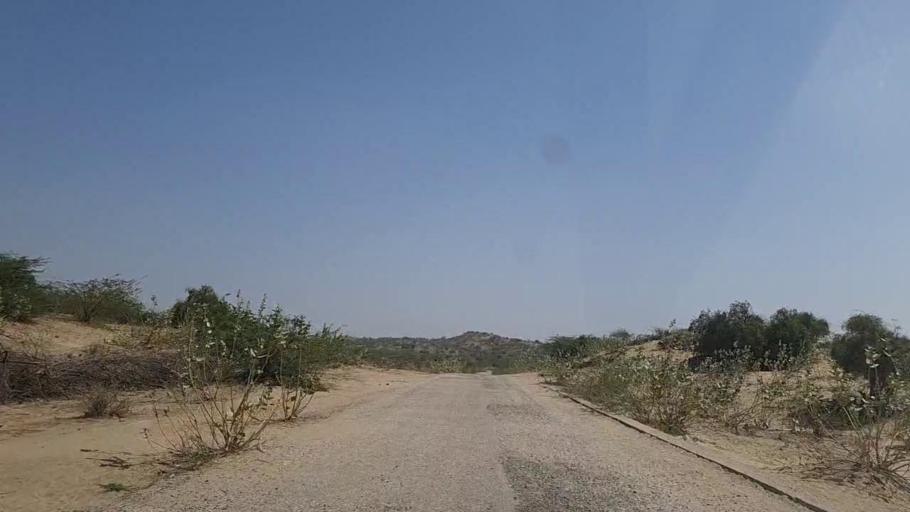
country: PK
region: Sindh
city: Diplo
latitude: 24.5138
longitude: 69.4141
